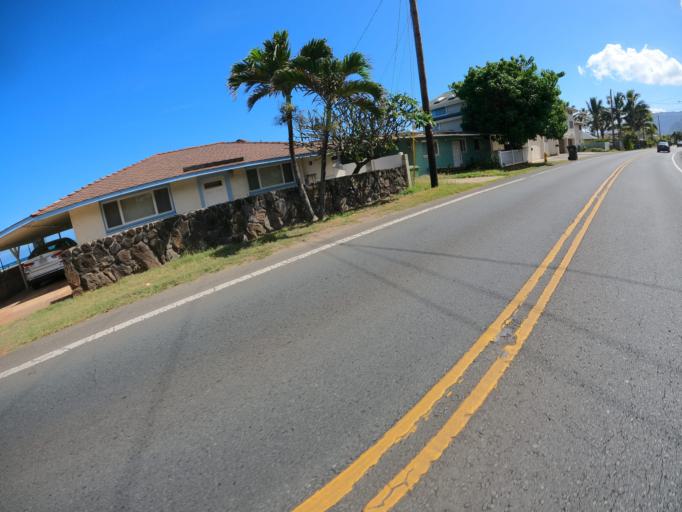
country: US
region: Hawaii
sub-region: Honolulu County
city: Hau'ula
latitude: 21.6028
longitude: -157.8988
